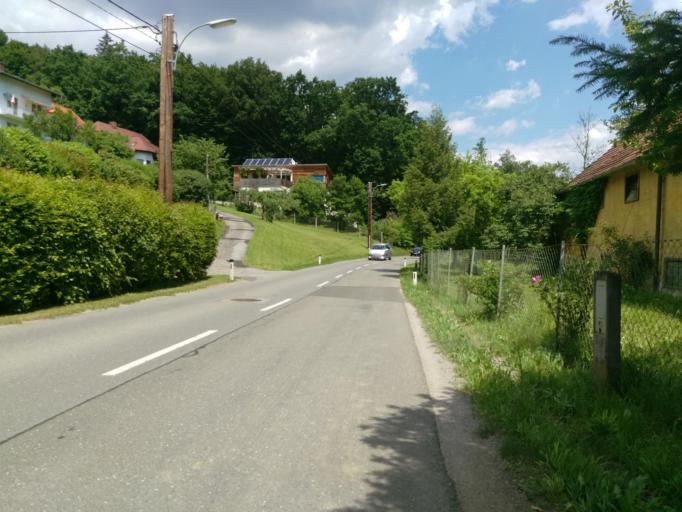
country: AT
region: Styria
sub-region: Graz Stadt
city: Mariatrost
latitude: 47.0961
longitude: 15.5006
